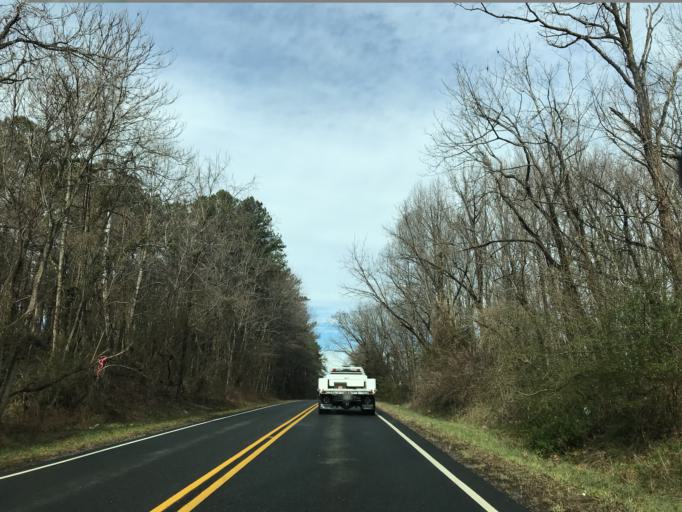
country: US
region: Virginia
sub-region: King George County
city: Dahlgren
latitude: 38.2984
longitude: -77.0715
